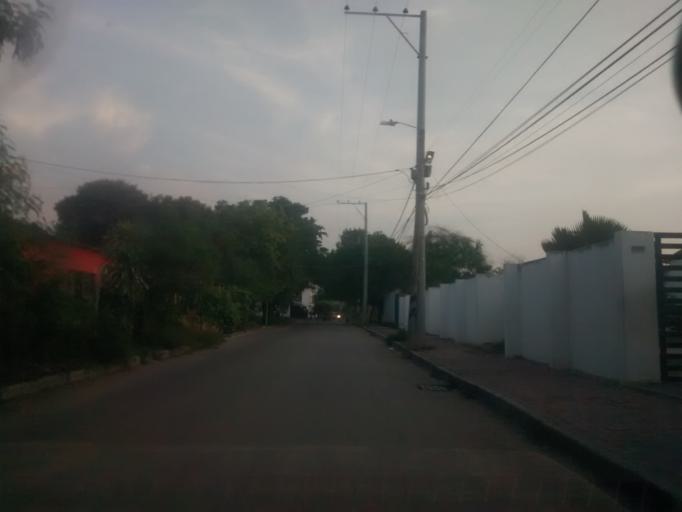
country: CO
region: Cundinamarca
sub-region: Girardot
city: Girardot City
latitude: 4.3194
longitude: -74.7843
